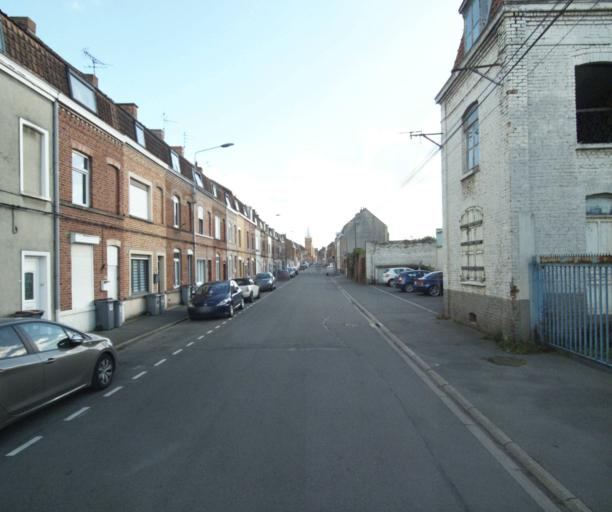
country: FR
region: Nord-Pas-de-Calais
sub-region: Departement du Nord
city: Houplines
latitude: 50.6904
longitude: 2.9002
